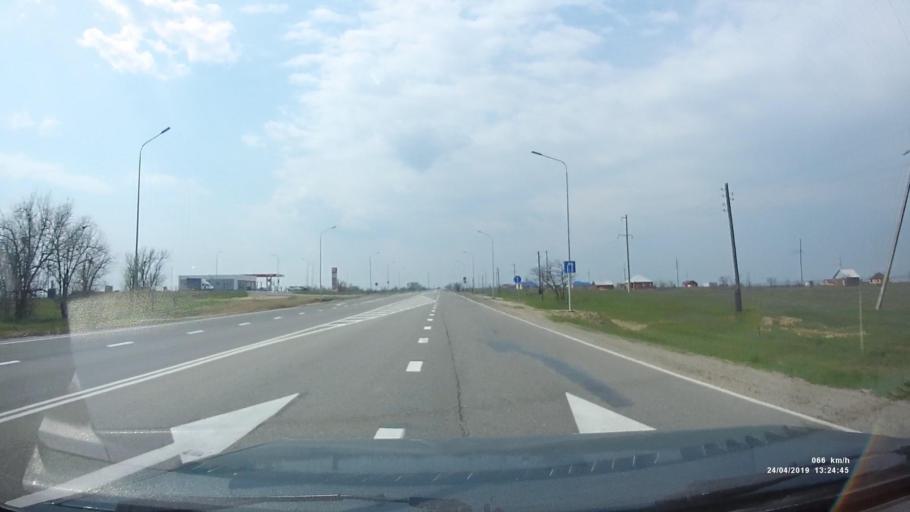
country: RU
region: Kalmykiya
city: Elista
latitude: 46.2849
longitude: 44.2505
